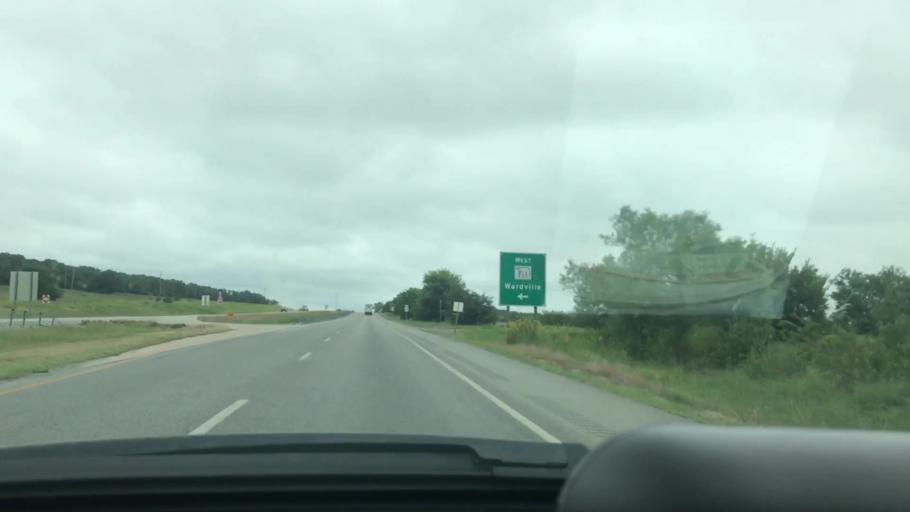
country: US
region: Oklahoma
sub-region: Coal County
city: Coalgate
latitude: 34.6653
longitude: -95.9381
